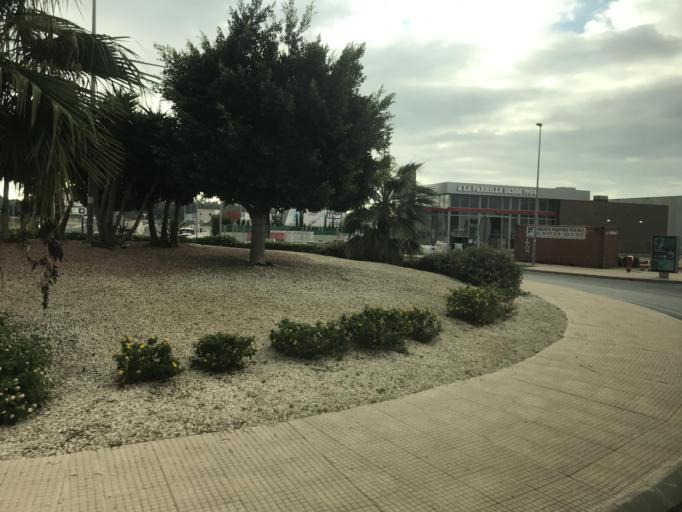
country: ES
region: Valencia
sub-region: Provincia de Alicante
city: Guardamar del Segura
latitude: 38.1197
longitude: -0.6569
